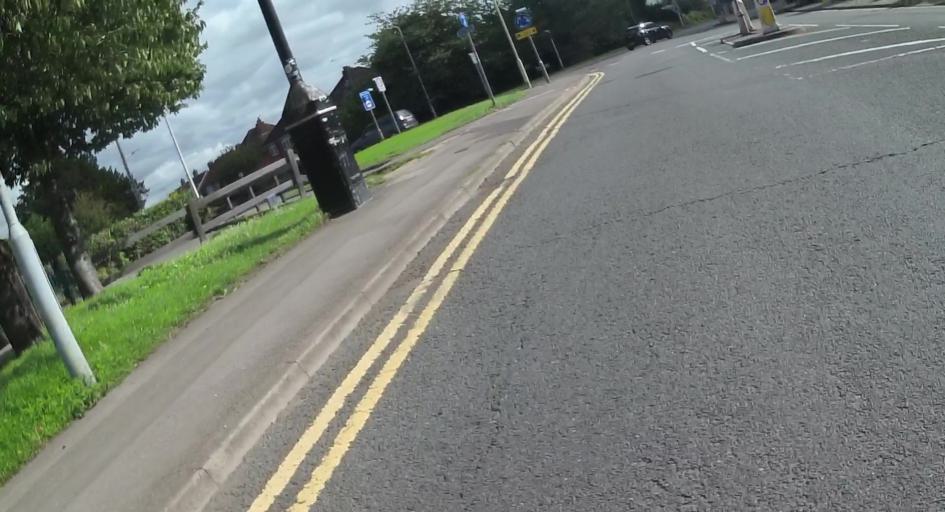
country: GB
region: England
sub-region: West Berkshire
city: Thatcham
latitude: 51.4015
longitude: -1.2544
